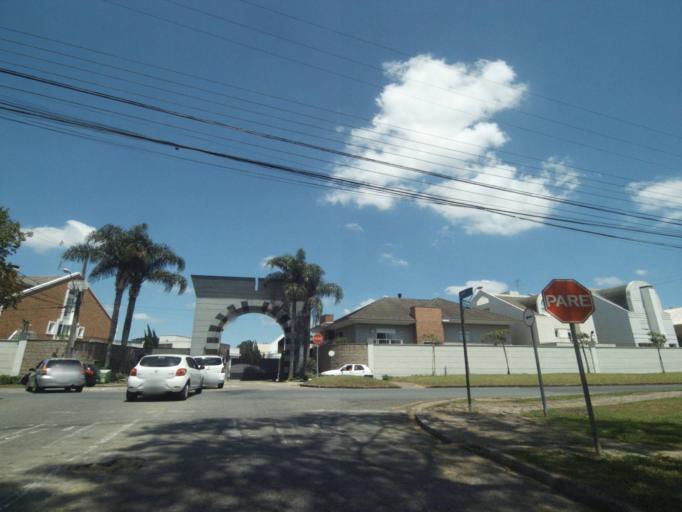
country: BR
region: Parana
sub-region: Curitiba
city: Curitiba
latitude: -25.4079
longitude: -49.2413
